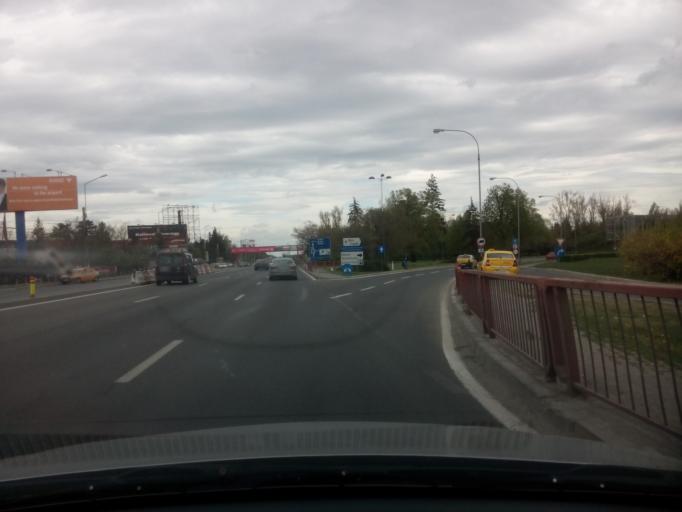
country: RO
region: Ilfov
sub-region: Comuna Otopeni
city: Otopeni
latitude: 44.5675
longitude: 26.0699
